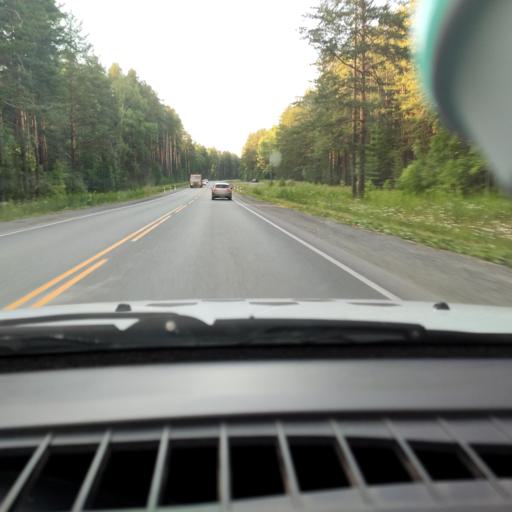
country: RU
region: Chelyabinsk
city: Turgoyak
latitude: 55.2750
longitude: 60.1972
